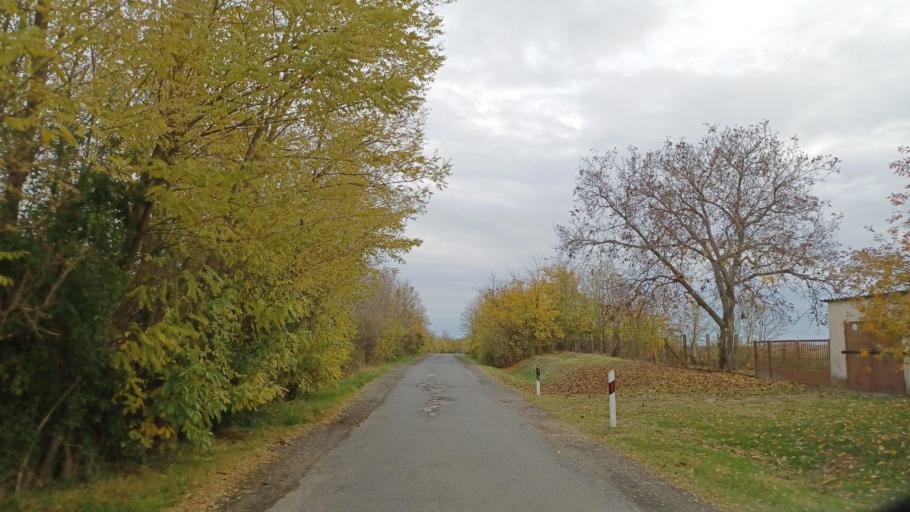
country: HU
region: Tolna
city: Simontornya
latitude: 46.6859
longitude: 18.5967
